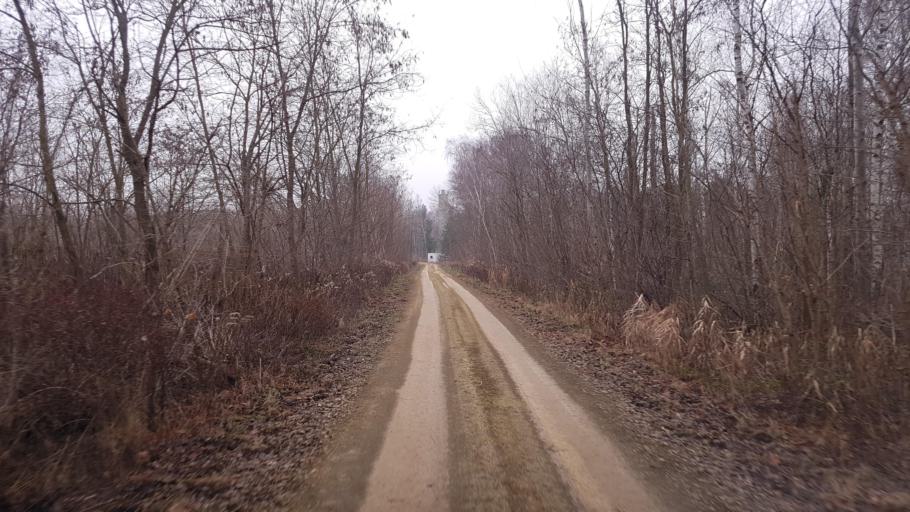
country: DE
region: Brandenburg
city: Plessa
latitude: 51.4956
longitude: 13.6564
